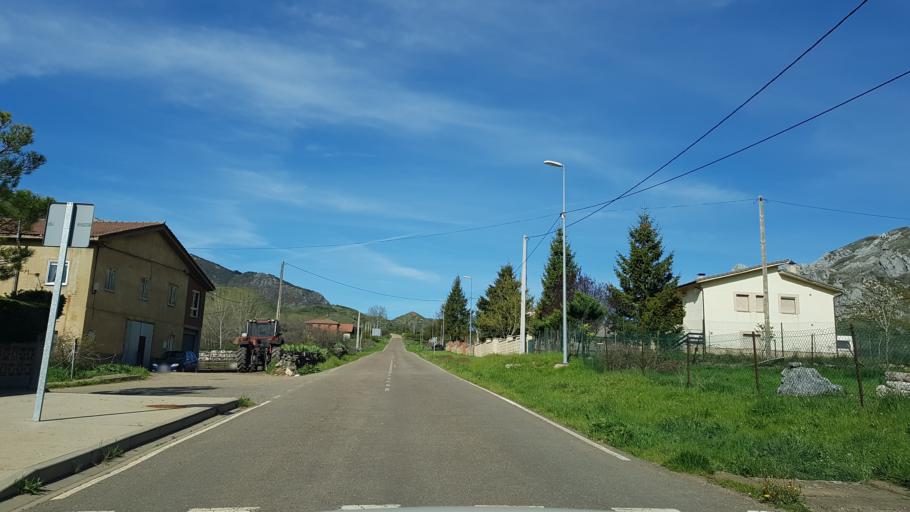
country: ES
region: Castille and Leon
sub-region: Provincia de Leon
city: Carmenes
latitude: 42.9584
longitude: -5.5792
